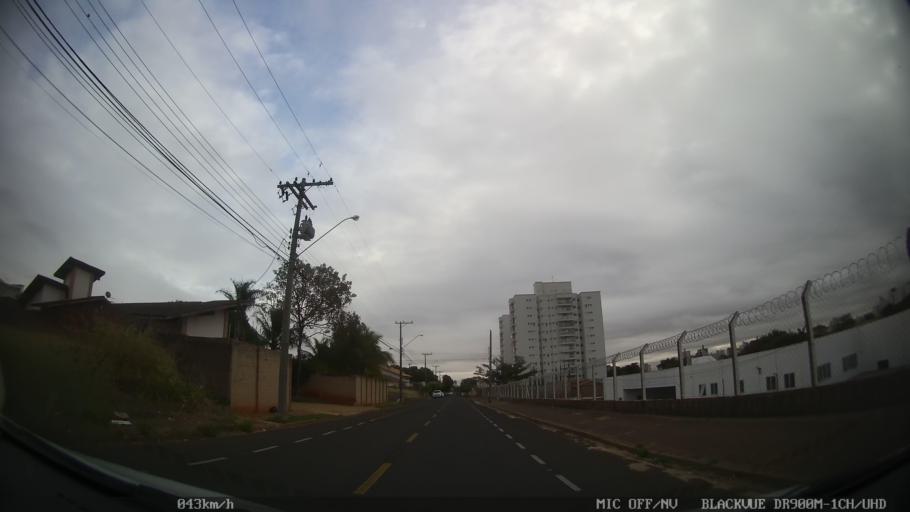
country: BR
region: Sao Paulo
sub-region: Sao Jose Do Rio Preto
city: Sao Jose do Rio Preto
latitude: -20.8403
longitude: -49.3956
